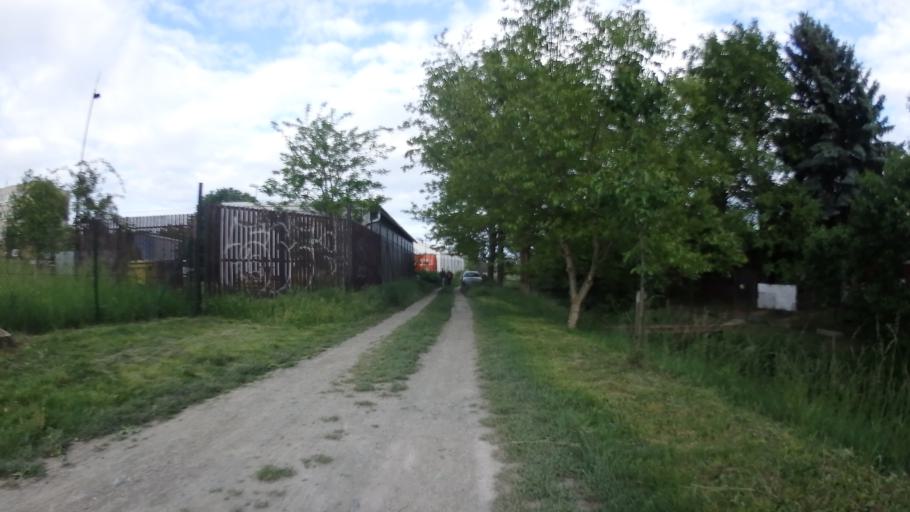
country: CZ
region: South Moravian
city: Moravany
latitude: 49.1628
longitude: 16.5895
